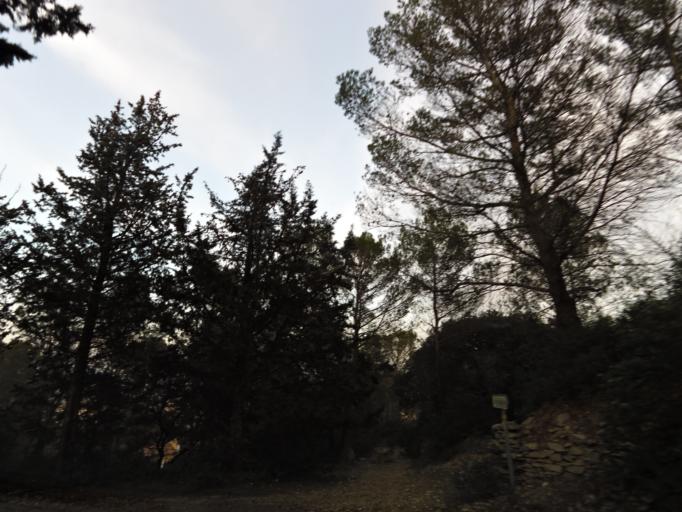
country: FR
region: Languedoc-Roussillon
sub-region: Departement du Gard
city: Calvisson
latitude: 43.7853
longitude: 4.1834
